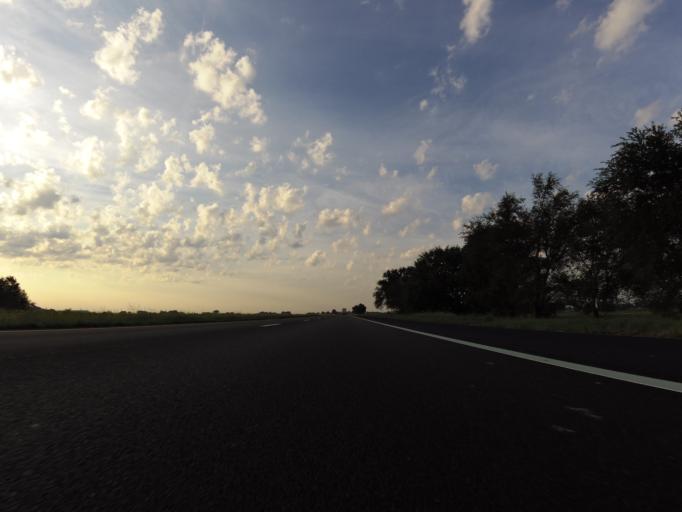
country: US
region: Kansas
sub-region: Sedgwick County
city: Colwich
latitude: 37.8656
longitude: -97.6213
